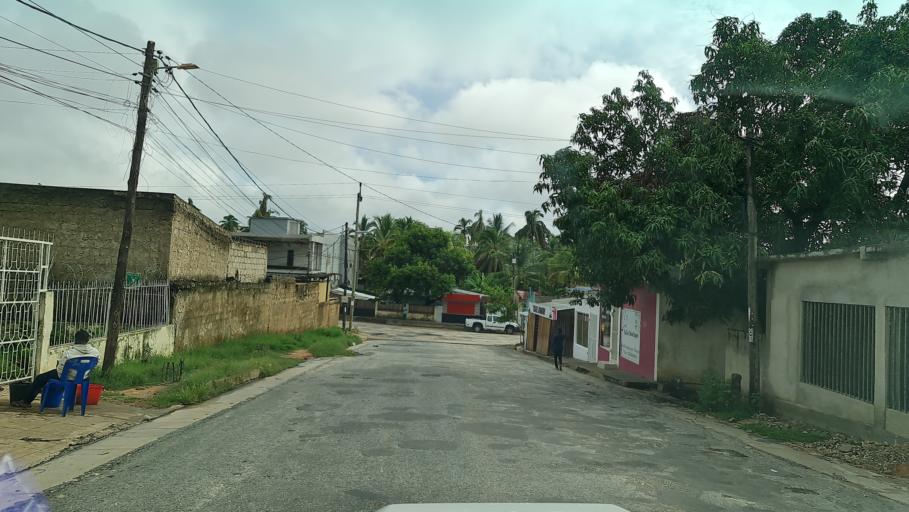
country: MZ
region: Nampula
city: Nampula
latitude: -15.1270
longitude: 39.2639
